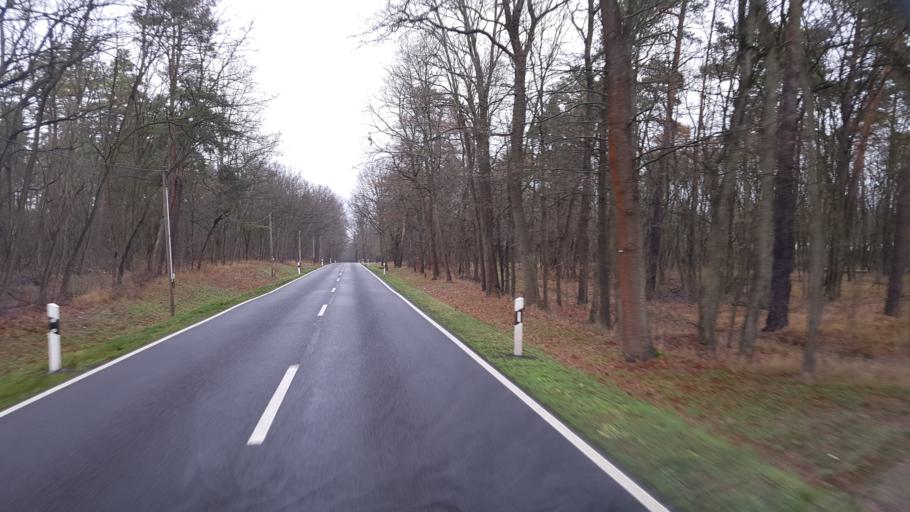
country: DE
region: Brandenburg
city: Altdobern
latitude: 51.6945
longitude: 14.0266
